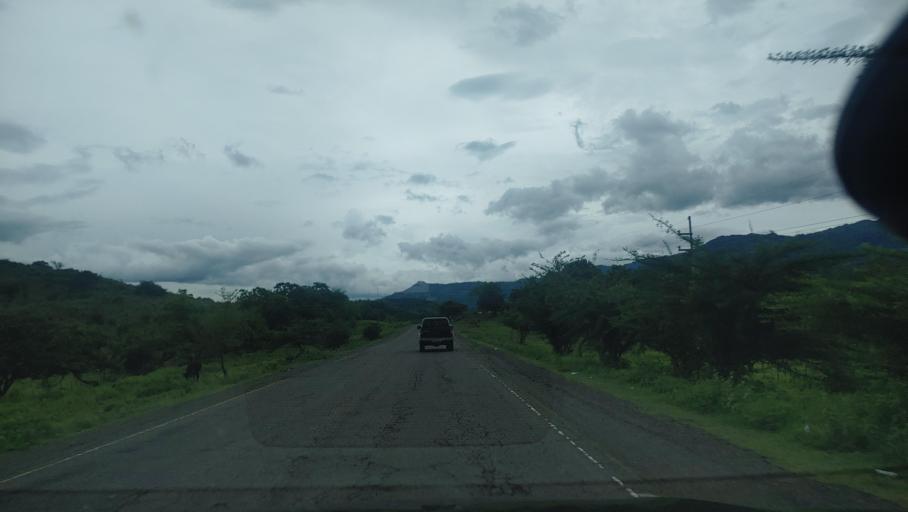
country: HN
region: Choluteca
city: Santa Ana de Yusguare
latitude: 13.3516
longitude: -87.1070
